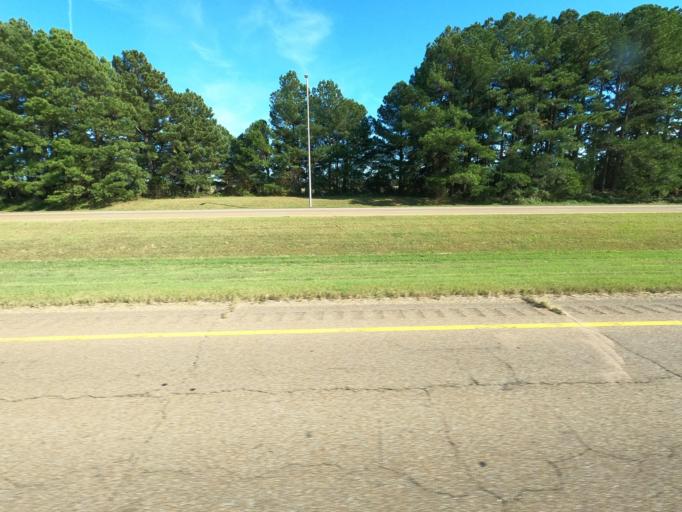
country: US
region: Tennessee
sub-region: Obion County
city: Union City
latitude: 36.4408
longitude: -89.0671
